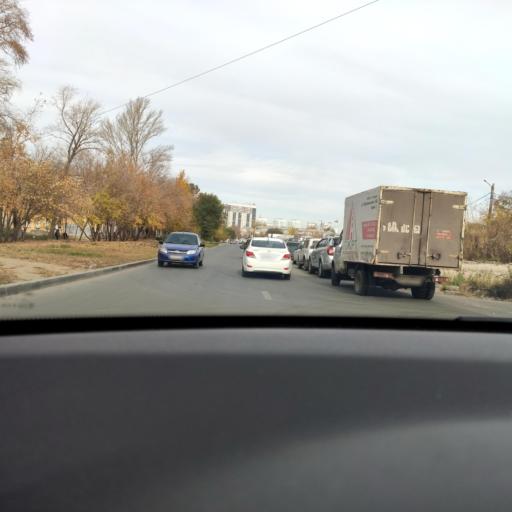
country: RU
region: Samara
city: Samara
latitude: 53.2080
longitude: 50.1939
